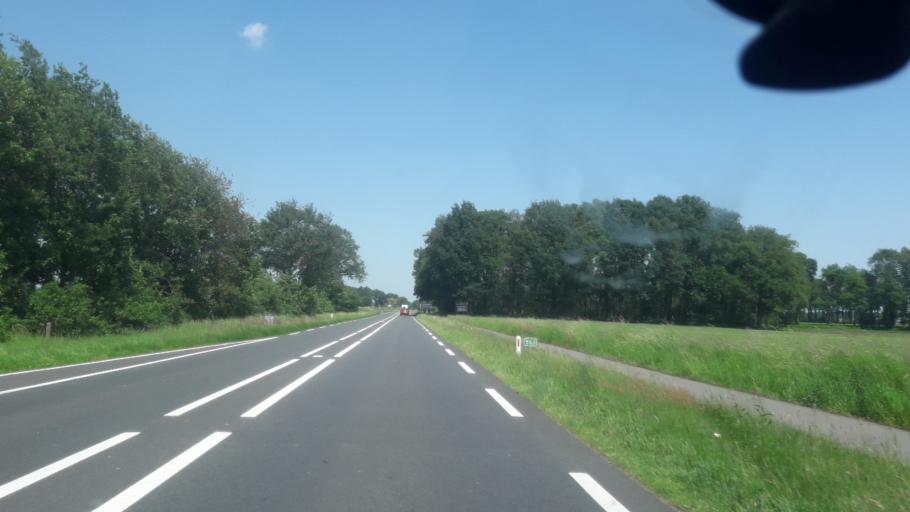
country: NL
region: Overijssel
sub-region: Gemeente Deventer
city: Schalkhaar
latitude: 52.3131
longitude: 6.2061
